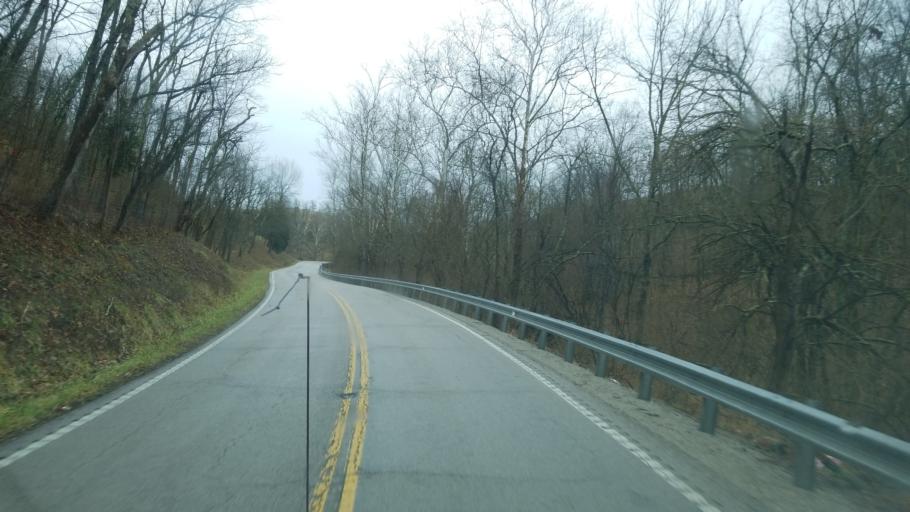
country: US
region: Kentucky
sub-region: Mason County
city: Maysville
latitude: 38.6071
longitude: -83.6866
